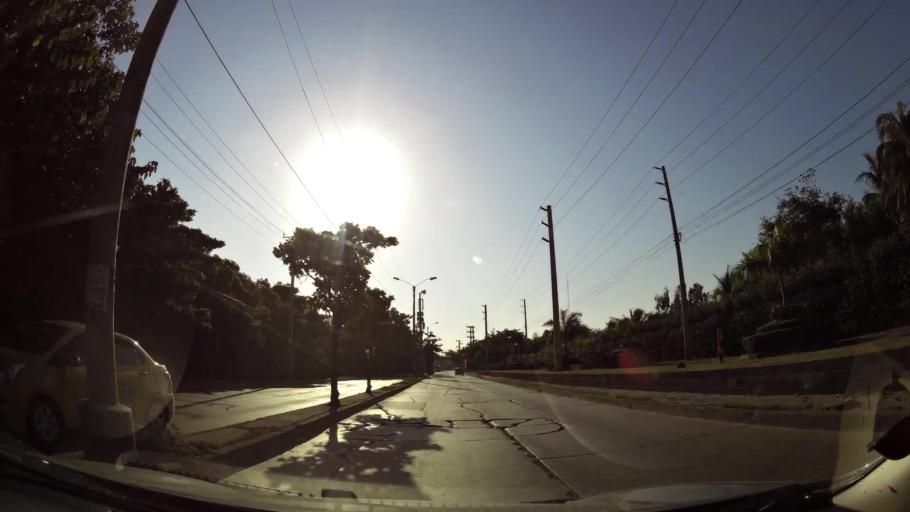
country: CO
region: Atlantico
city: Barranquilla
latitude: 11.0320
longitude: -74.8095
